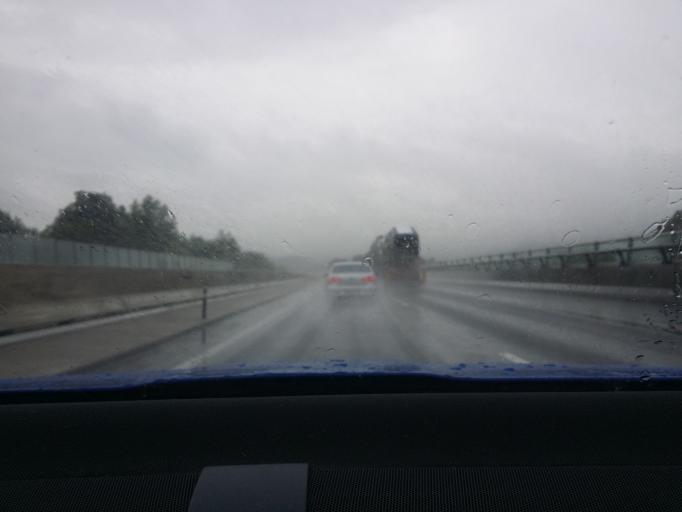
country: AT
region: Salzburg
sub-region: Politischer Bezirk Hallein
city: Kuchl
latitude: 47.6348
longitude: 13.1333
